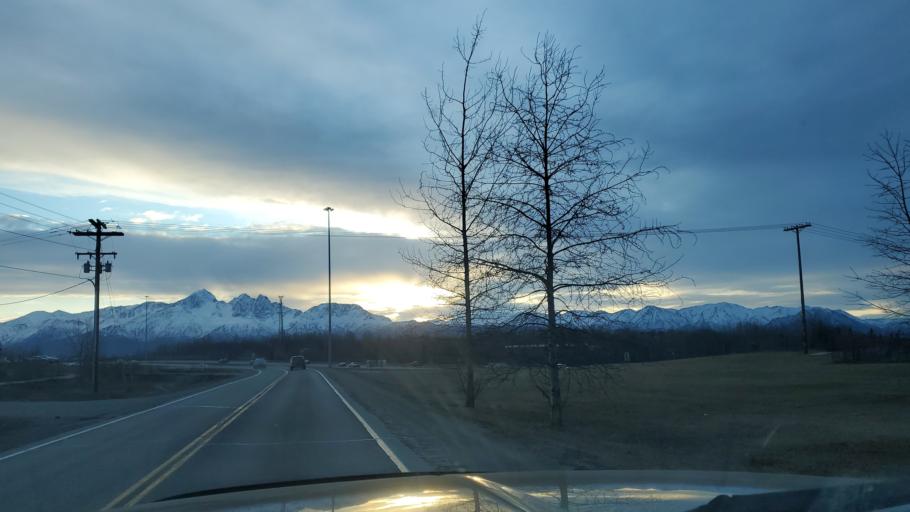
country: US
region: Alaska
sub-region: Matanuska-Susitna Borough
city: Lakes
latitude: 61.5674
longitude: -149.3087
